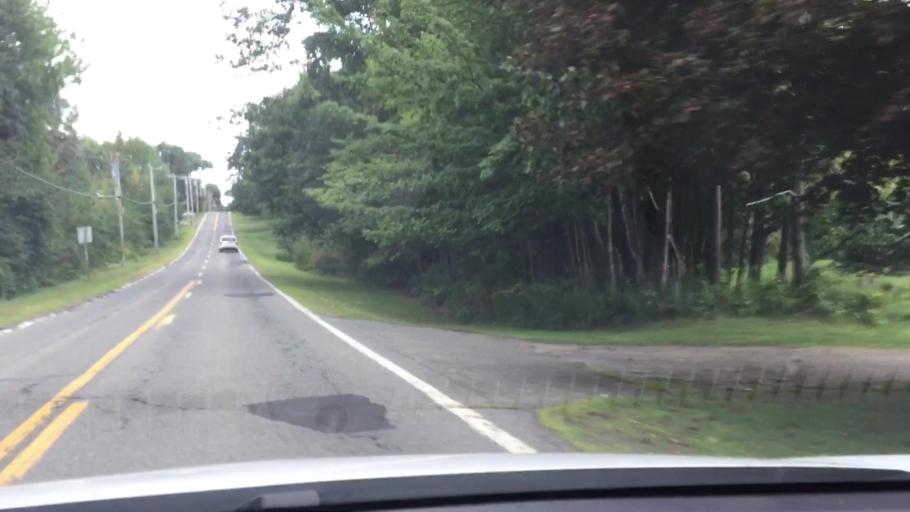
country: US
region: Massachusetts
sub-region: Hampden County
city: Granville
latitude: 42.1923
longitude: -72.9341
